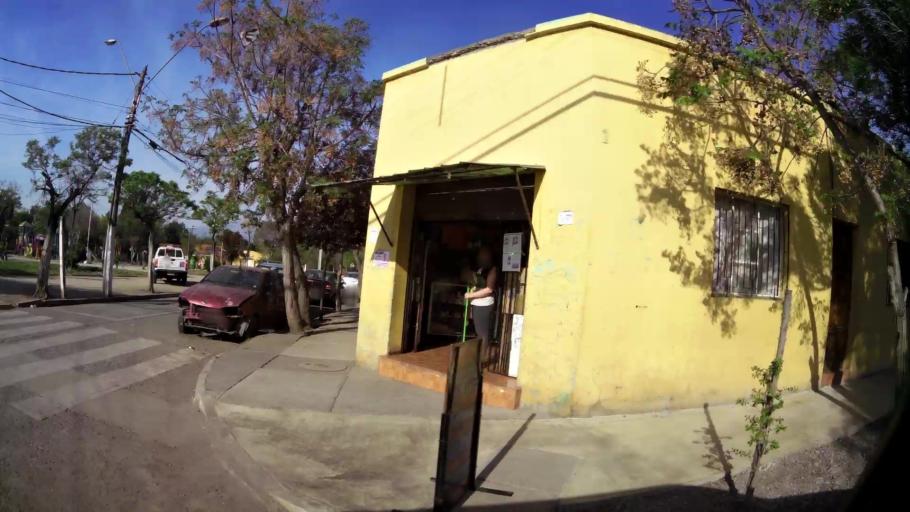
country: CL
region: Santiago Metropolitan
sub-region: Provincia de Santiago
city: Santiago
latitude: -33.5133
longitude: -70.6311
